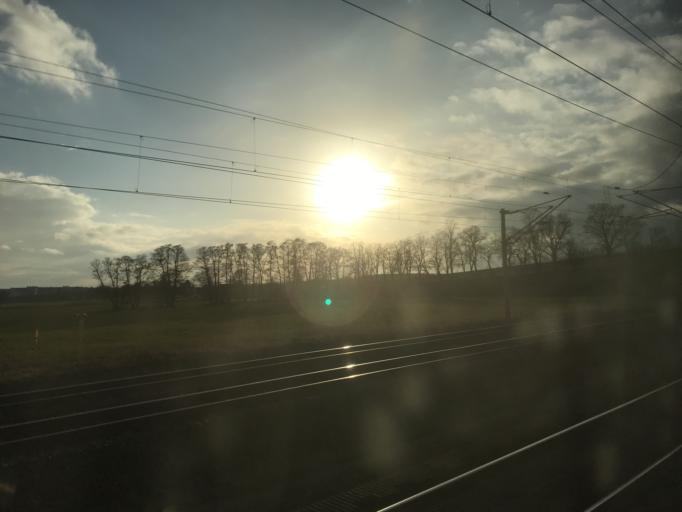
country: DE
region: Brandenburg
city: Falkensee
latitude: 52.5414
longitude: 13.0918
